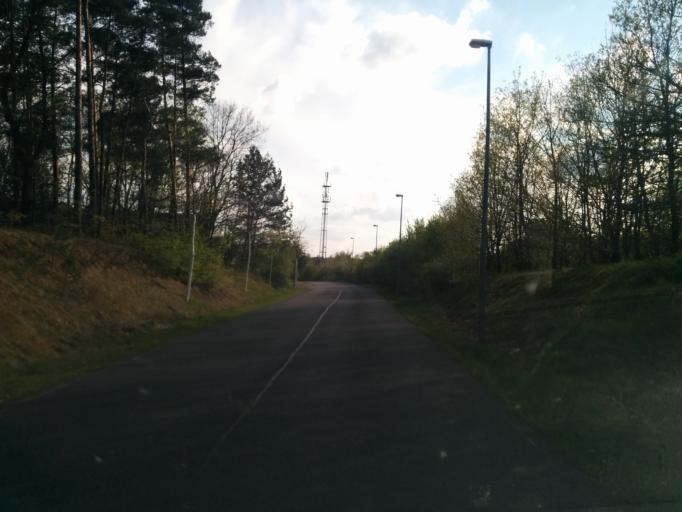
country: DE
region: Berlin
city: Nikolassee
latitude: 52.4045
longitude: 13.1905
